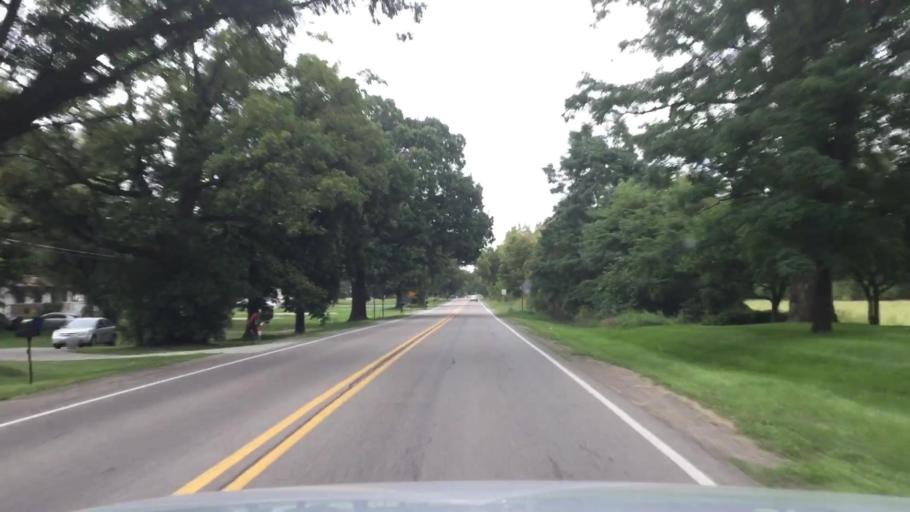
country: US
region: Michigan
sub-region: Genesee County
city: Linden
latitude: 42.8419
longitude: -83.7831
